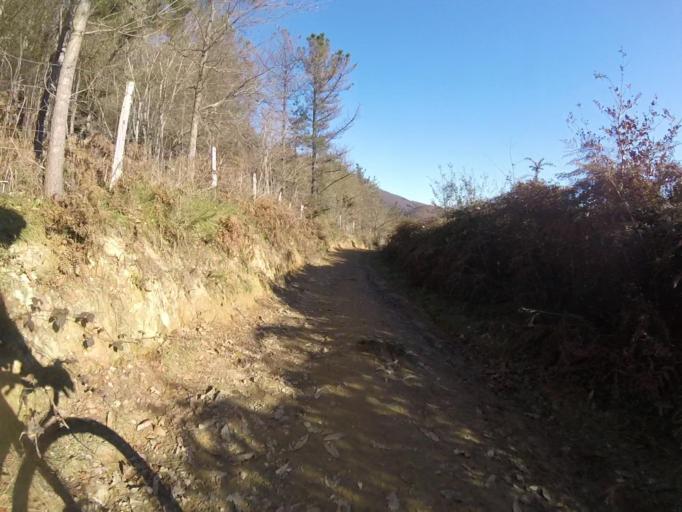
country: ES
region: Navarre
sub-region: Provincia de Navarra
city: Bera
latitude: 43.3003
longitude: -1.6787
